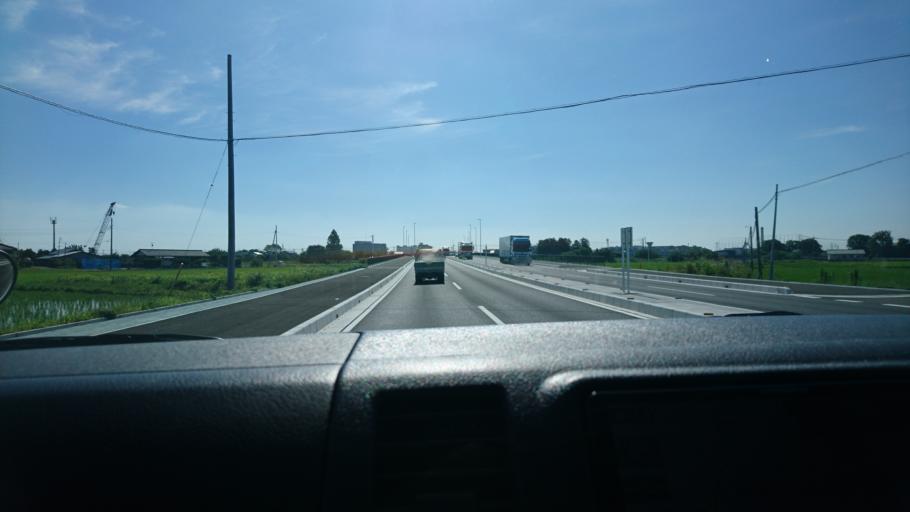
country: JP
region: Saitama
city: Kurihashi
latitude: 36.1248
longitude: 139.6543
